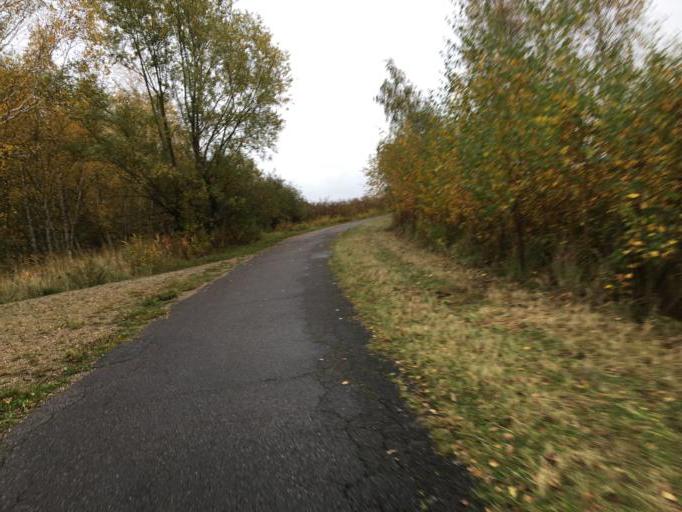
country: DK
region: Capital Region
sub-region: Frederiksberg Kommune
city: Frederiksberg
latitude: 55.6155
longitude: 12.5350
